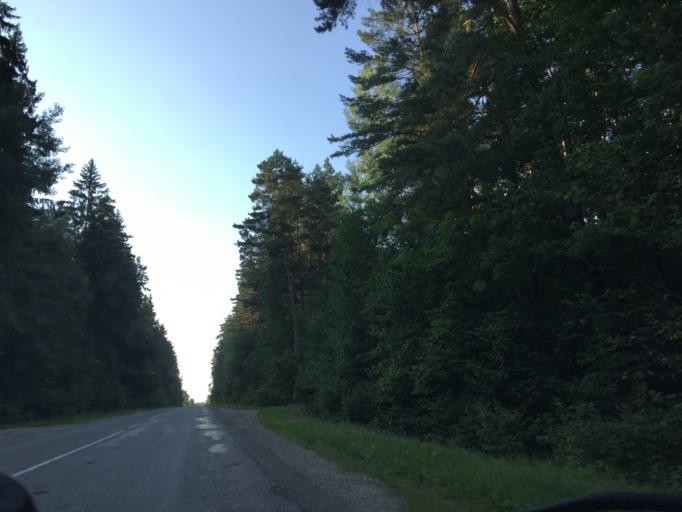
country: LV
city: Tervete
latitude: 56.4625
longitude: 23.4044
